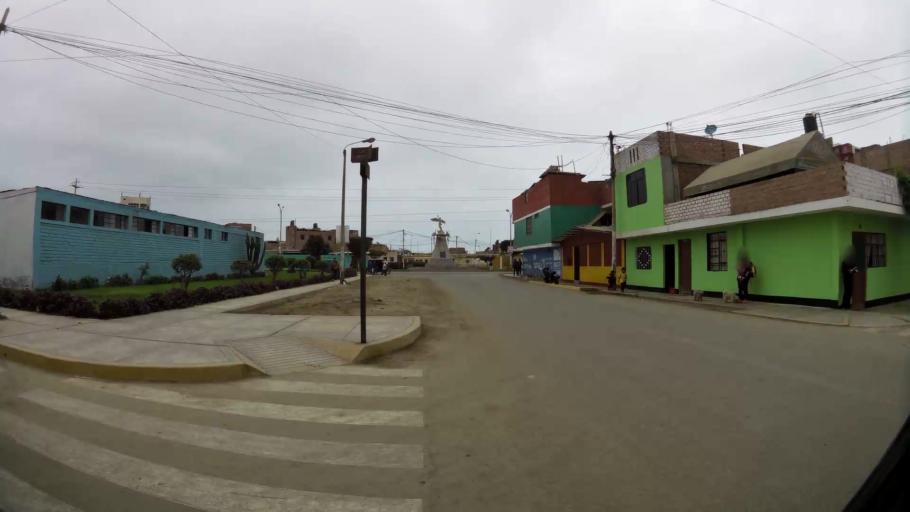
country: PE
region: Lima
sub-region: Barranca
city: Paramonga
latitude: -10.6741
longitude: -77.8164
